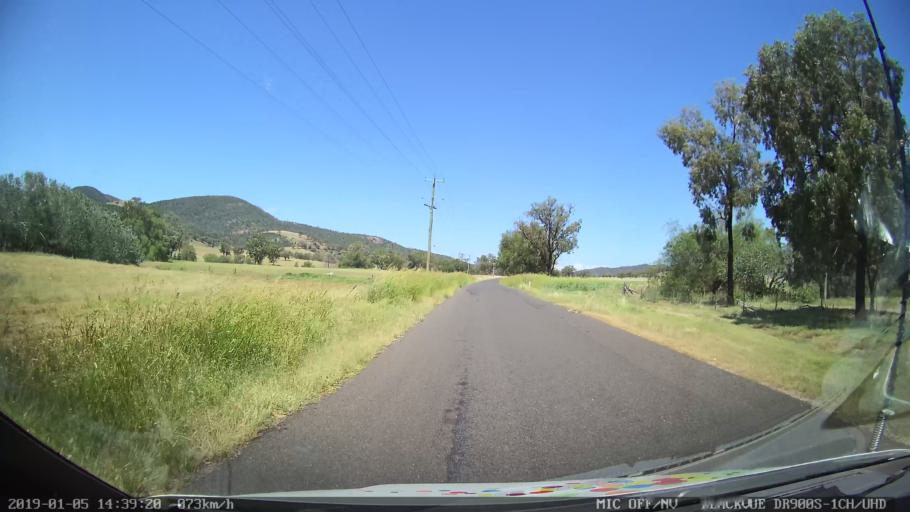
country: AU
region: New South Wales
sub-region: Tamworth Municipality
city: Phillip
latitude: -31.2542
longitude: 150.6990
